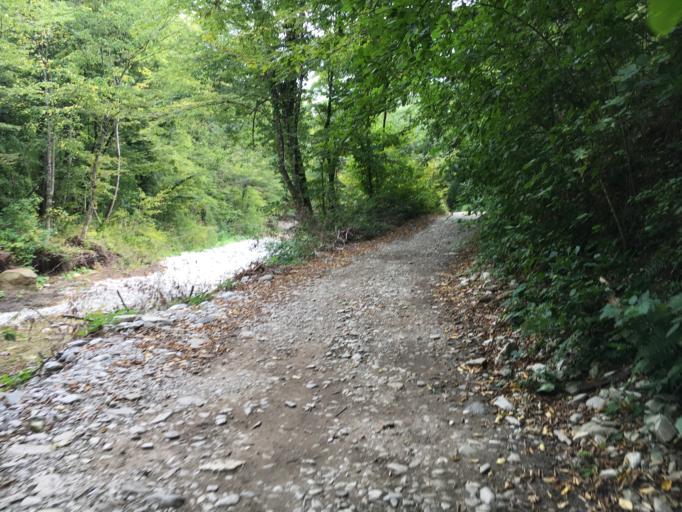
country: RU
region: Krasnodarskiy
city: Tuapse
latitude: 44.2606
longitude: 39.2166
